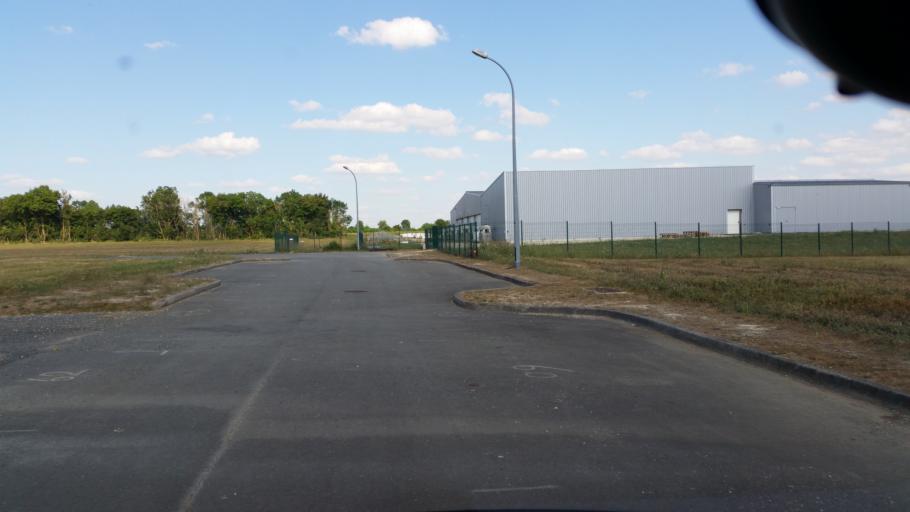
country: FR
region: Poitou-Charentes
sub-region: Departement de la Charente-Maritime
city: Saint-Jean-de-Liversay
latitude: 46.2328
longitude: -0.8832
